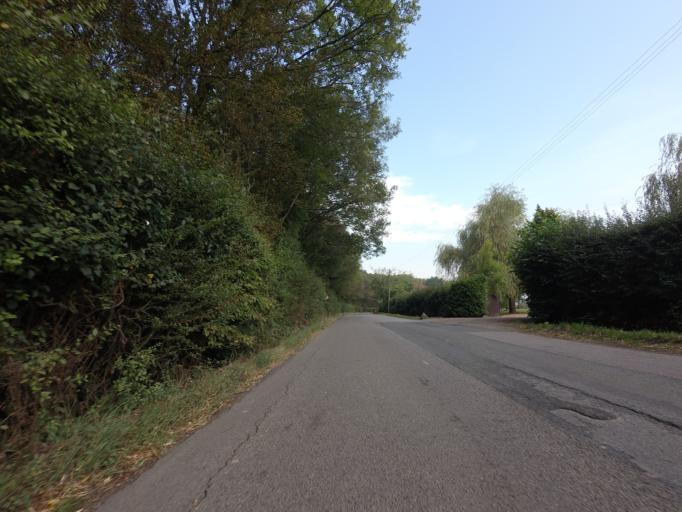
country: GB
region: England
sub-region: Kent
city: Ashford
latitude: 51.1057
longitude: 0.7945
